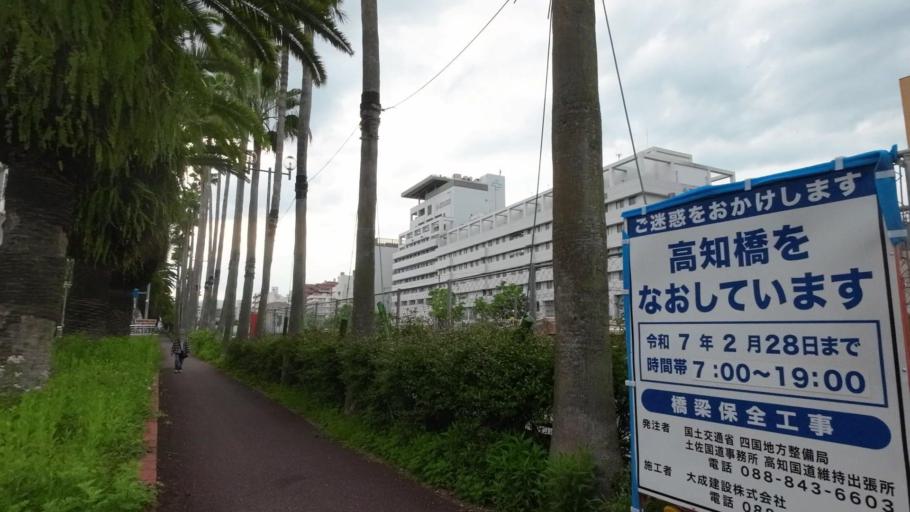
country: JP
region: Kochi
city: Kochi-shi
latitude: 33.5637
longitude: 133.5431
